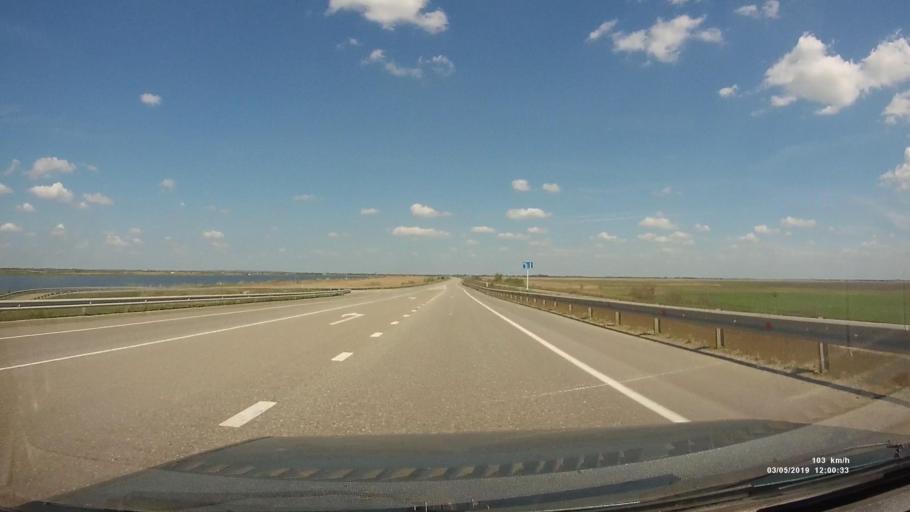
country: RU
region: Rostov
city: Bagayevskaya
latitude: 47.2504
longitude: 40.3413
